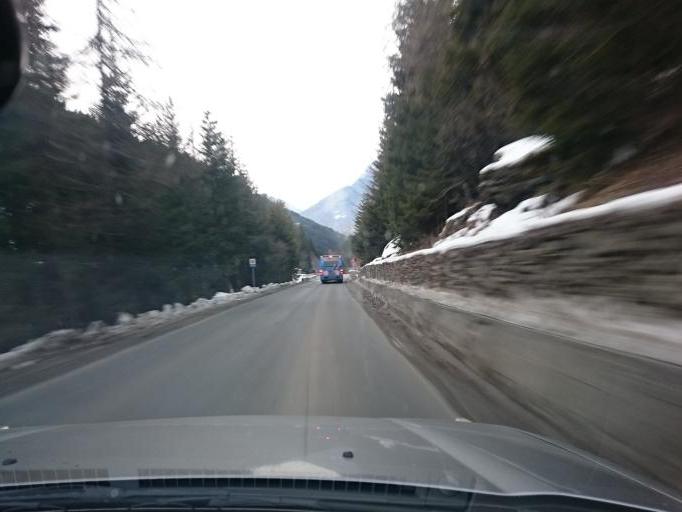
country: IT
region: Lombardy
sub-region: Provincia di Sondrio
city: Sant'Antonio
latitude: 46.4369
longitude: 10.4529
